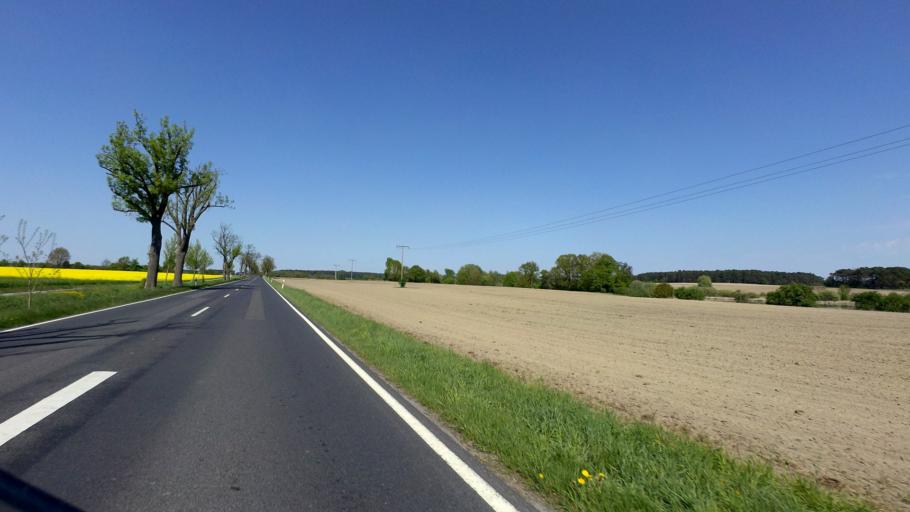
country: DE
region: Brandenburg
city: Friedland
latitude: 52.1237
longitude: 14.2566
